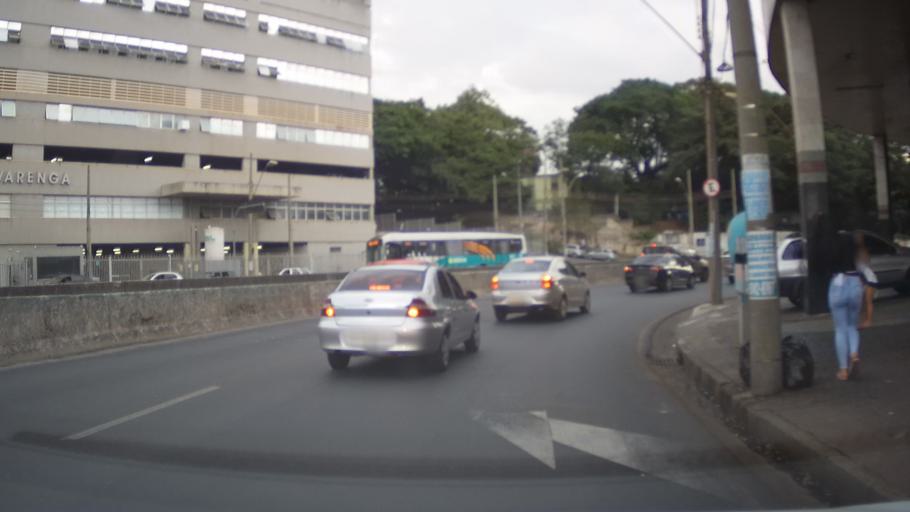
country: BR
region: Minas Gerais
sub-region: Belo Horizonte
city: Belo Horizonte
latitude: -19.9211
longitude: -43.9245
